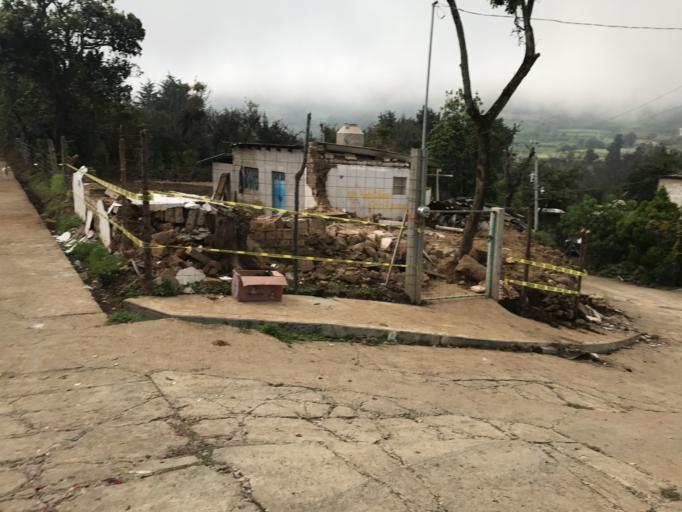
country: MX
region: Morelos
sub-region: Ocuituco
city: Huepalcalco (San Miguel)
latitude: 18.9164
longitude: -98.7439
